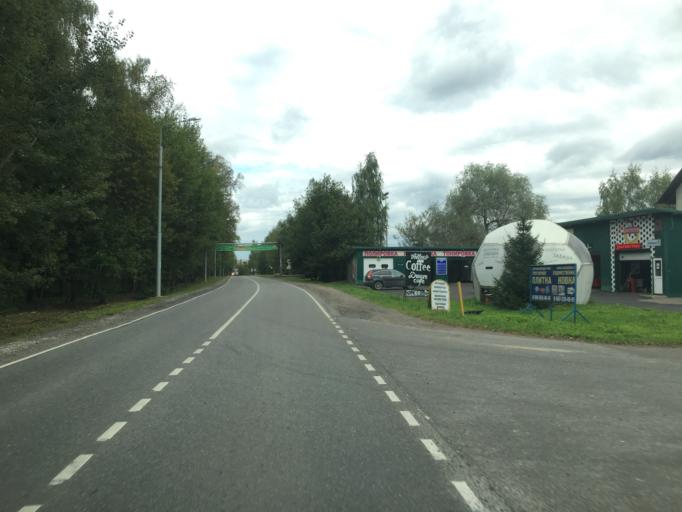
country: RU
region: Moskovskaya
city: Vatutinki
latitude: 55.5064
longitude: 37.3685
